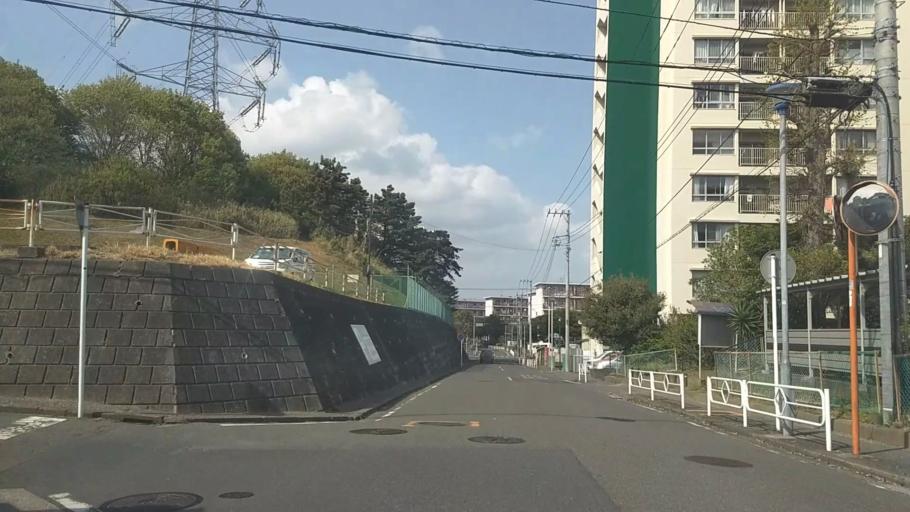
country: JP
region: Kanagawa
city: Kamakura
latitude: 35.3848
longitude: 139.5683
